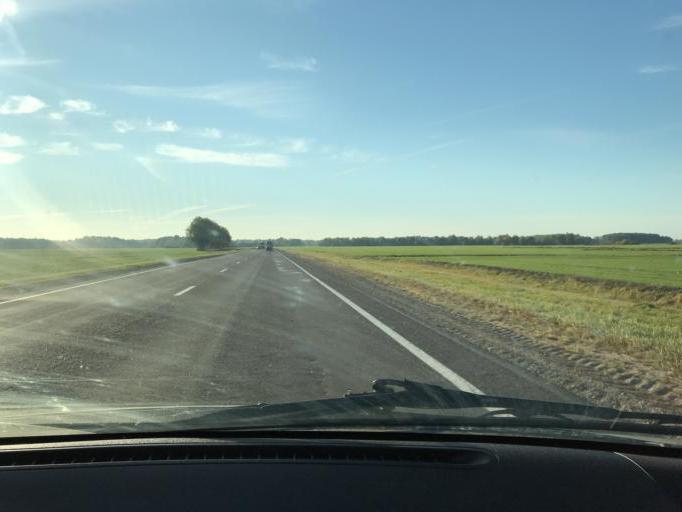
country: BY
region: Brest
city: Antopal'
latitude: 52.2072
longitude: 24.5876
